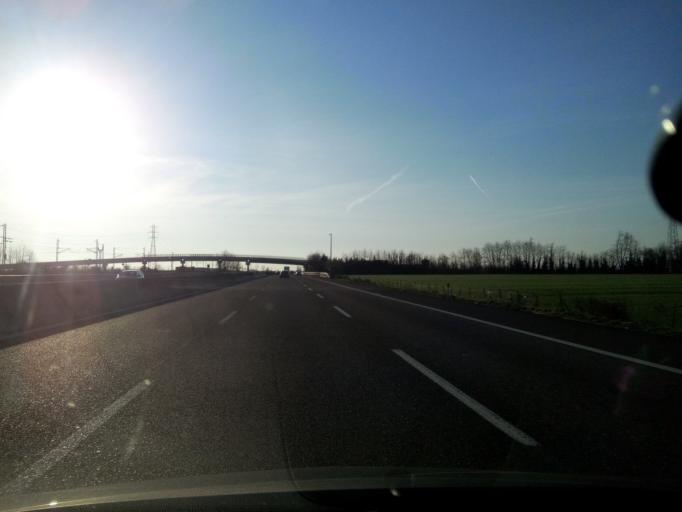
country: IT
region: Emilia-Romagna
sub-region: Provincia di Piacenza
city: Pontenure
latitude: 44.9983
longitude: 9.8192
